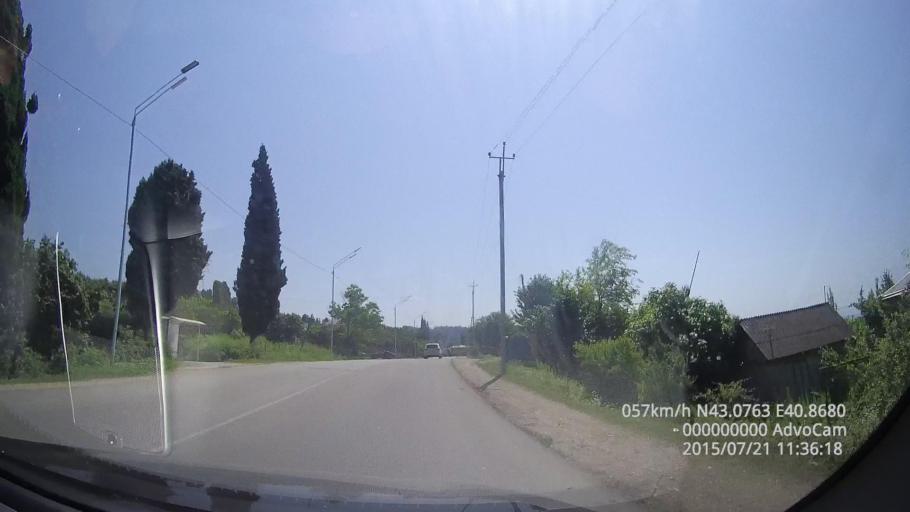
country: GE
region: Abkhazia
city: Stantsiya Novyy Afon
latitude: 43.0763
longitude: 40.8685
